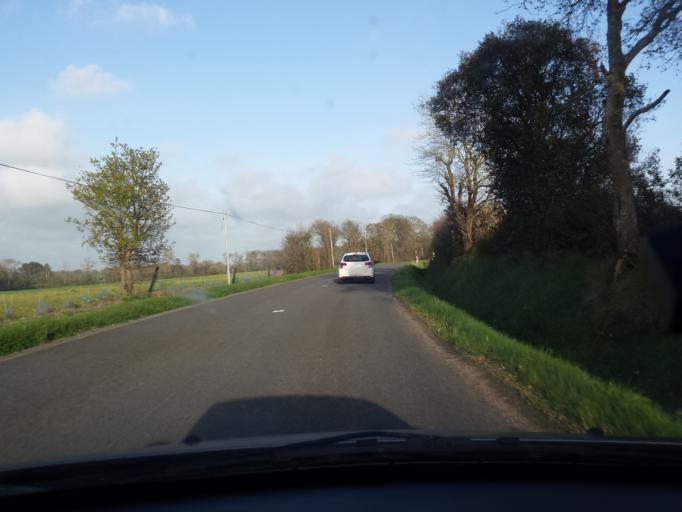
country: FR
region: Pays de la Loire
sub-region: Departement de la Vendee
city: Vaire
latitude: 46.5704
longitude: -1.7571
